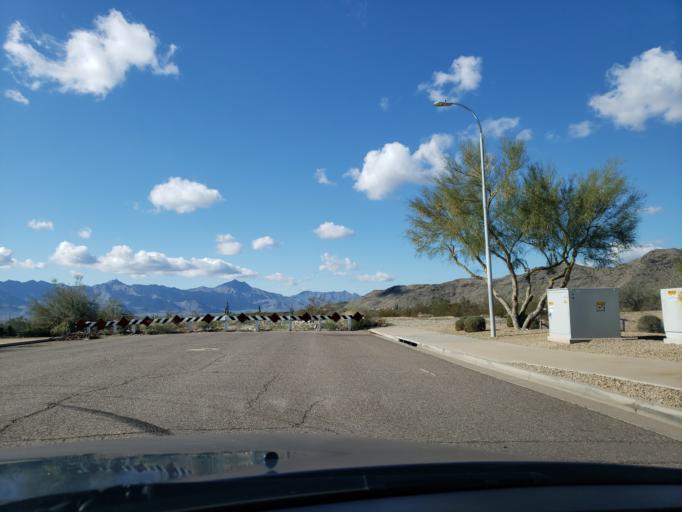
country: US
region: Arizona
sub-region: Maricopa County
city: Laveen
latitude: 33.2946
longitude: -112.1001
